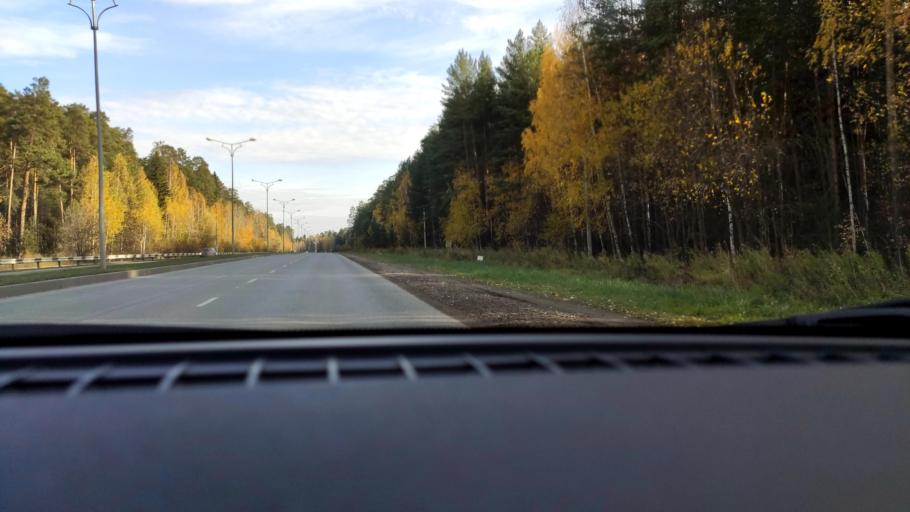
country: RU
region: Perm
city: Kondratovo
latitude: 58.0173
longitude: 55.9845
